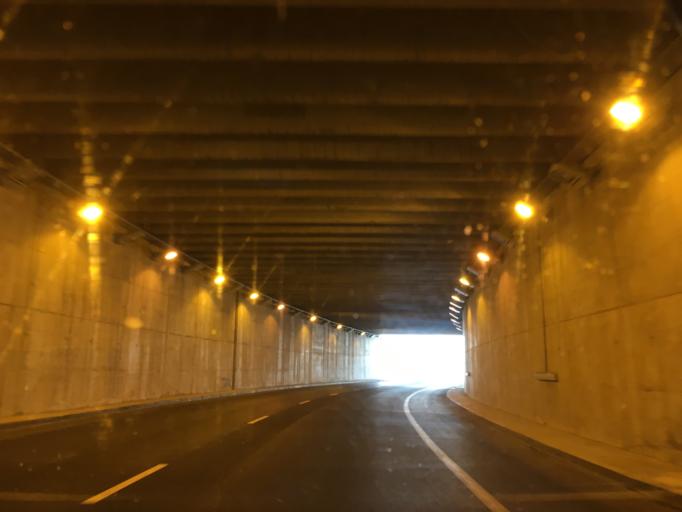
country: ES
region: Madrid
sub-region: Provincia de Madrid
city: Hortaleza
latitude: 40.4818
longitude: -3.6180
